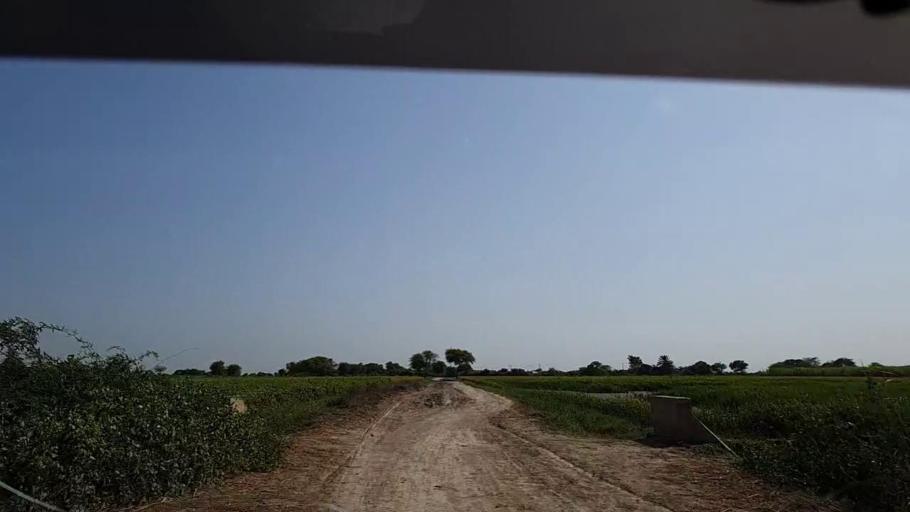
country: PK
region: Sindh
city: Badin
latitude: 24.6216
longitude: 68.7814
